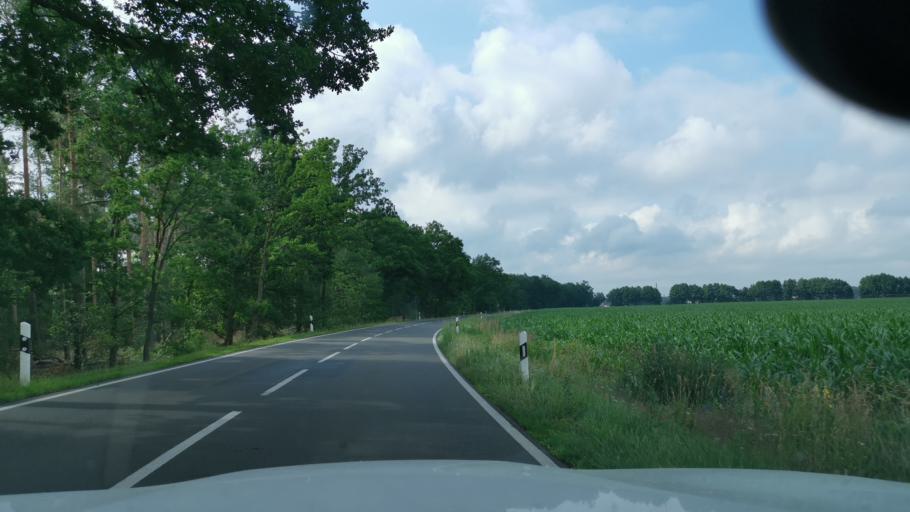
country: DE
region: Saxony-Anhalt
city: Annaburg
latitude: 51.7521
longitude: 13.0430
